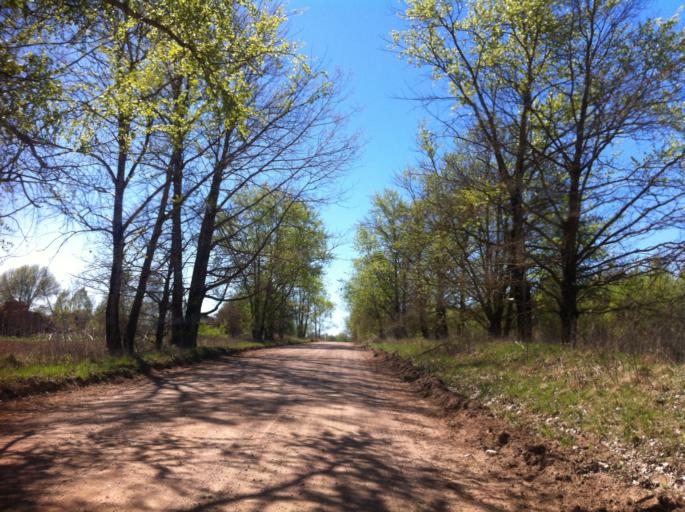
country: RU
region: Pskov
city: Izborsk
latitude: 57.7918
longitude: 27.9633
